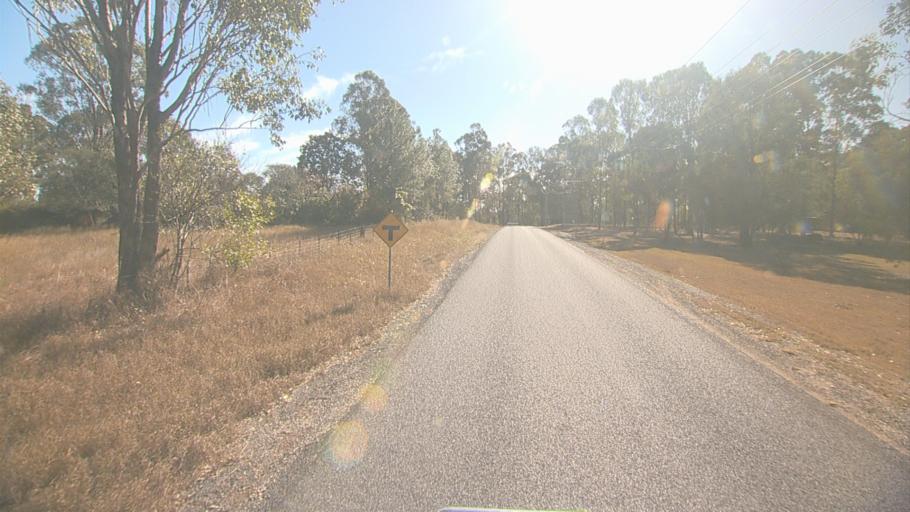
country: AU
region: Queensland
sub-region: Logan
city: Cedar Vale
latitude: -27.8633
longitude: 152.9850
